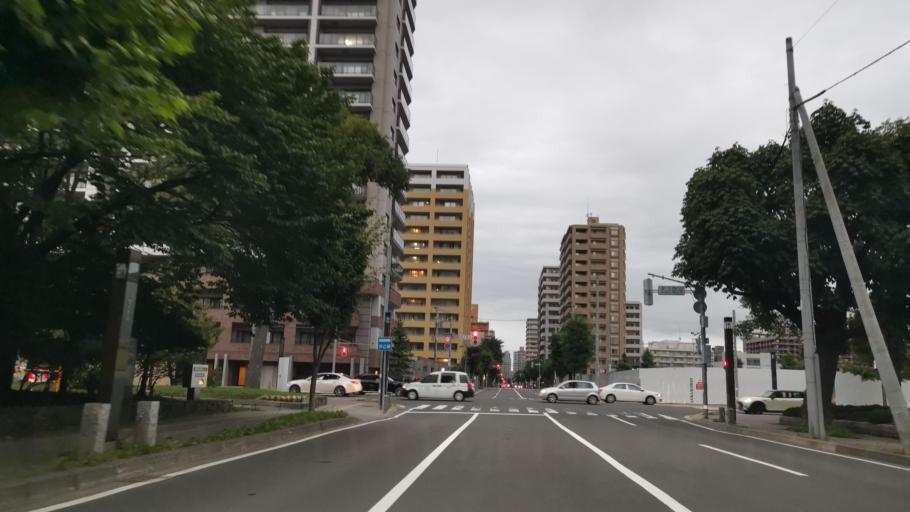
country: JP
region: Hokkaido
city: Sapporo
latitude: 43.0596
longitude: 141.3378
